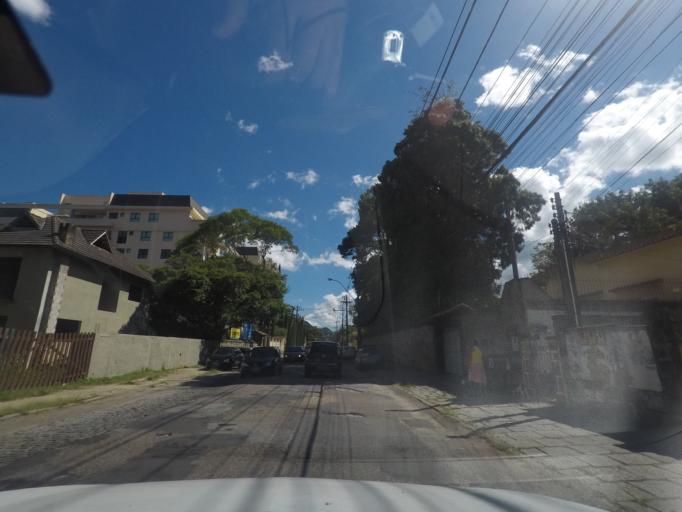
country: BR
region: Rio de Janeiro
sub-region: Teresopolis
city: Teresopolis
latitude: -22.4371
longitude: -42.9768
